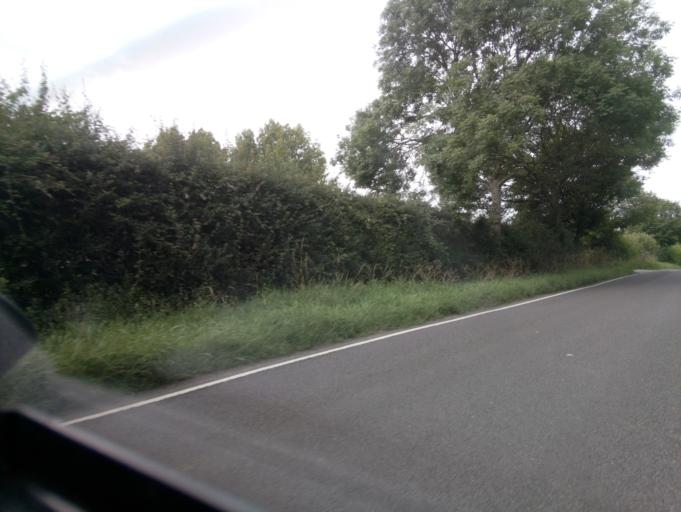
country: GB
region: England
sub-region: Somerset
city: Street
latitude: 51.0927
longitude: -2.6893
